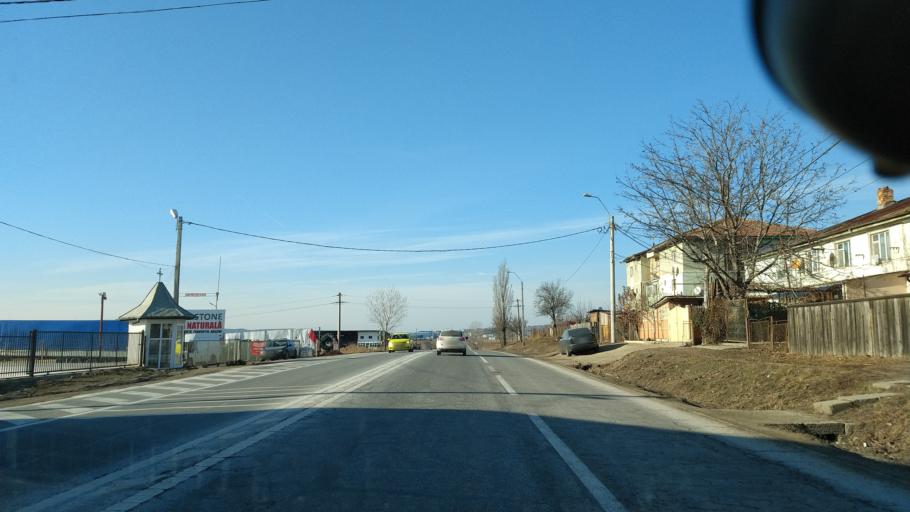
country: RO
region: Iasi
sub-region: Comuna Letcani
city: Letcani
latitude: 47.1860
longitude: 27.4493
